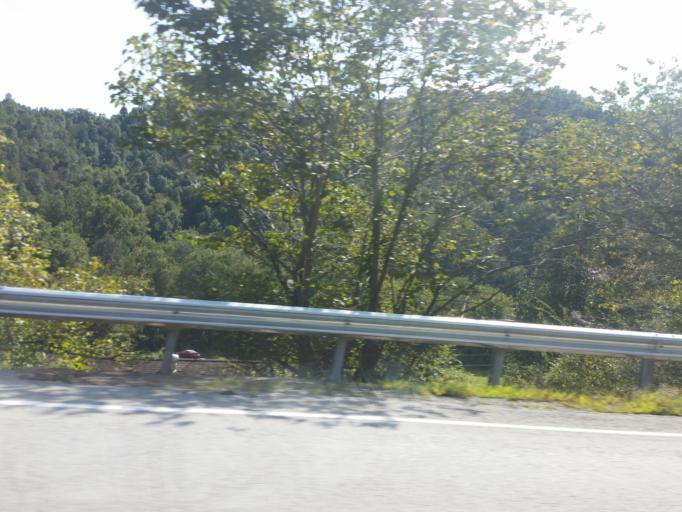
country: US
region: Kentucky
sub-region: Bell County
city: Pineville
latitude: 36.7311
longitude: -83.6687
